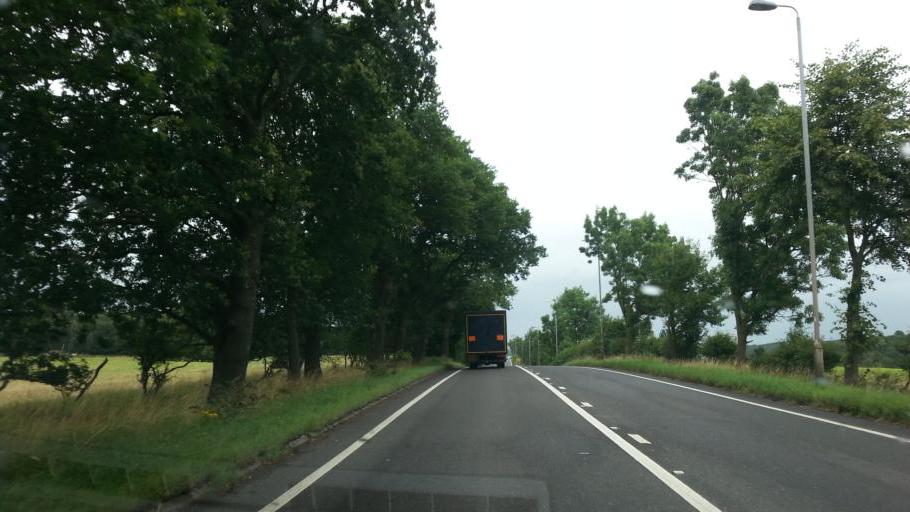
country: GB
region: England
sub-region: Nottinghamshire
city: Bilsthorpe
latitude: 53.1471
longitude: -1.0478
